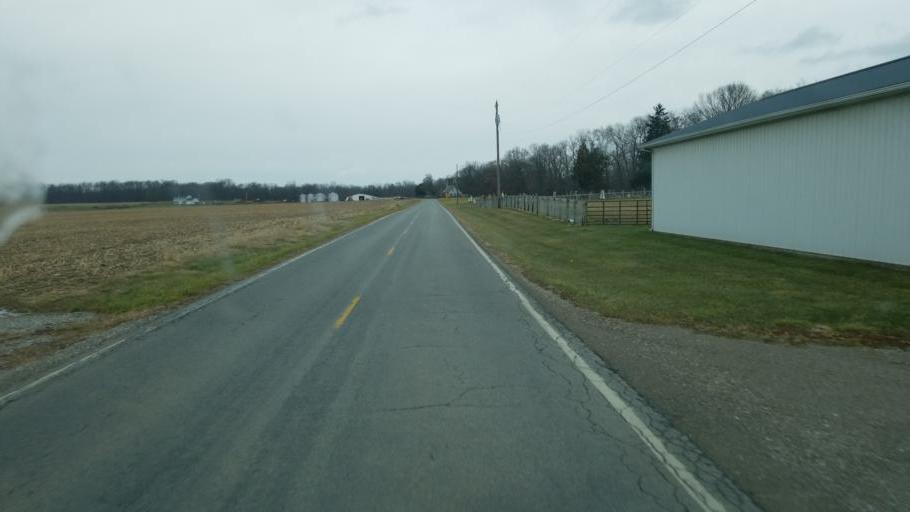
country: US
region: Ohio
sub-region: Delaware County
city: Ashley
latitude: 40.3361
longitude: -82.9560
